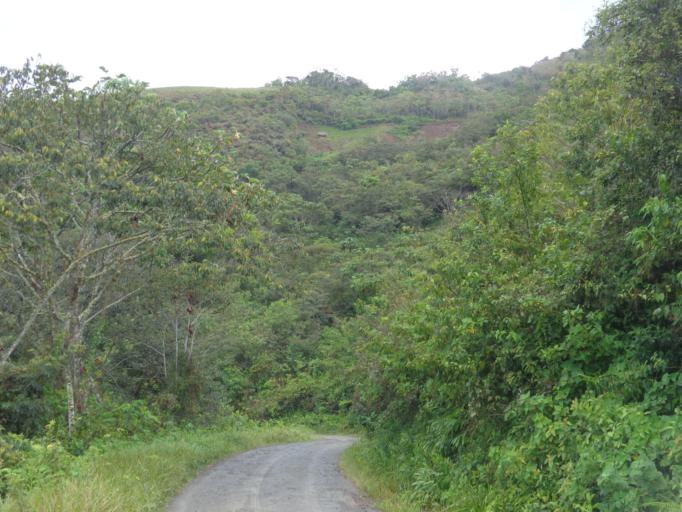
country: BO
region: La Paz
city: Coroico
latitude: -16.1355
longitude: -67.7501
